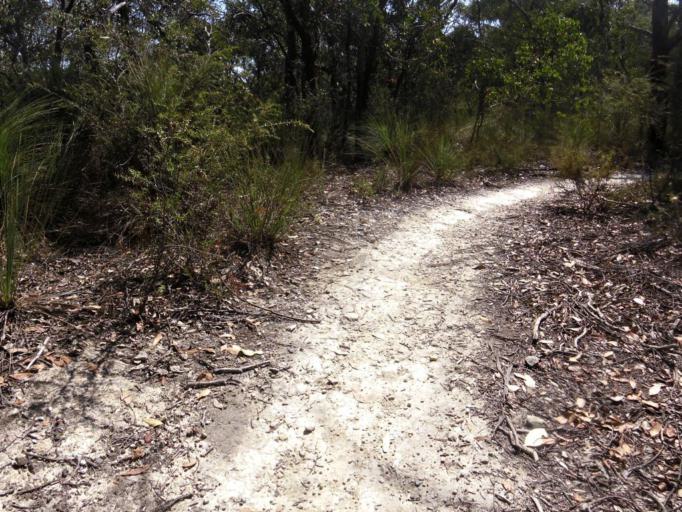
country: AU
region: Victoria
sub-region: Melton
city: Melton West
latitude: -37.5104
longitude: 144.5525
